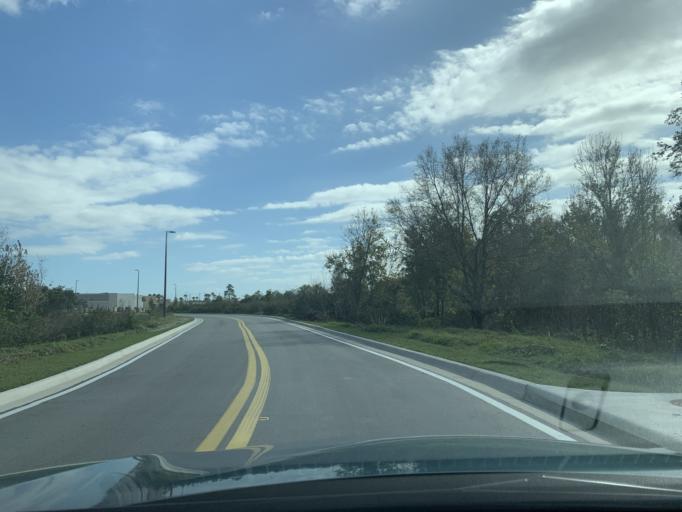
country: US
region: Florida
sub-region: Pasco County
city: Trinity
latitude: 28.2037
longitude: -82.6706
